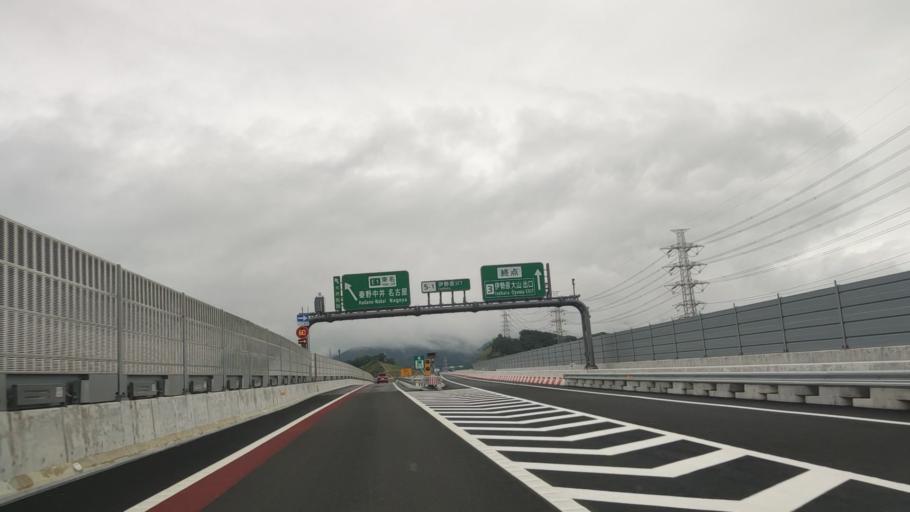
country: JP
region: Kanagawa
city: Isehara
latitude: 35.4101
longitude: 139.3158
